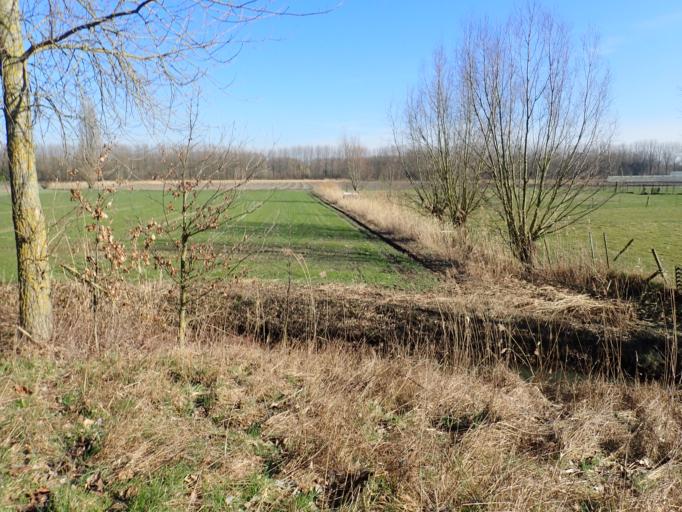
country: BE
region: Flanders
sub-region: Provincie Antwerpen
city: Sint-Amands
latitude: 51.0547
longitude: 4.1667
